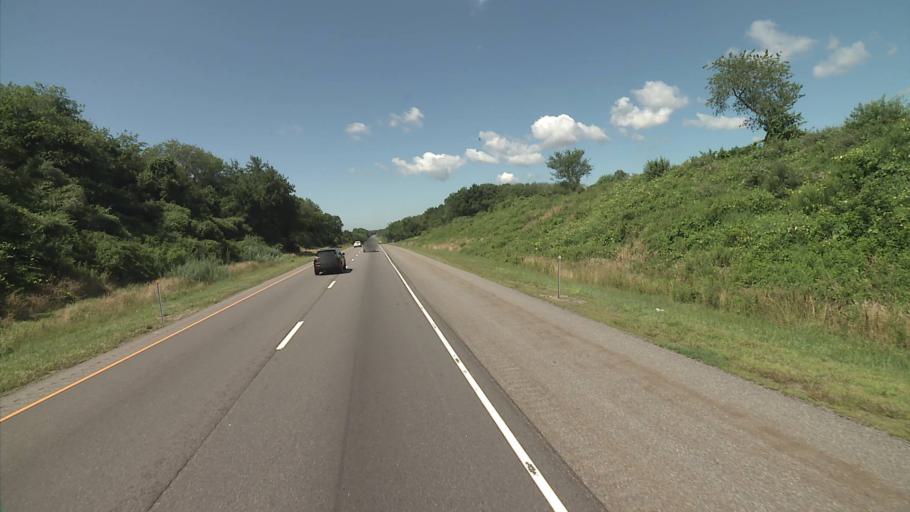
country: US
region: Connecticut
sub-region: New London County
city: Pawcatuck
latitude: 41.3855
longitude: -71.8898
